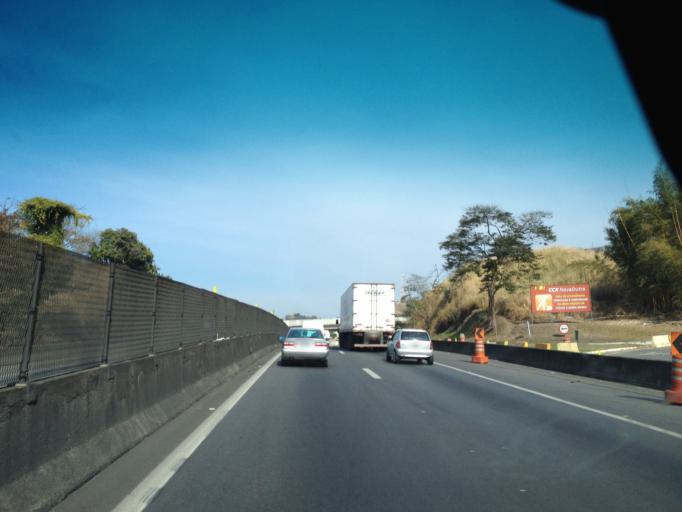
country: BR
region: Rio de Janeiro
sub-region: Barra Mansa
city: Barra Mansa
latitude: -22.5620
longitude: -44.1667
